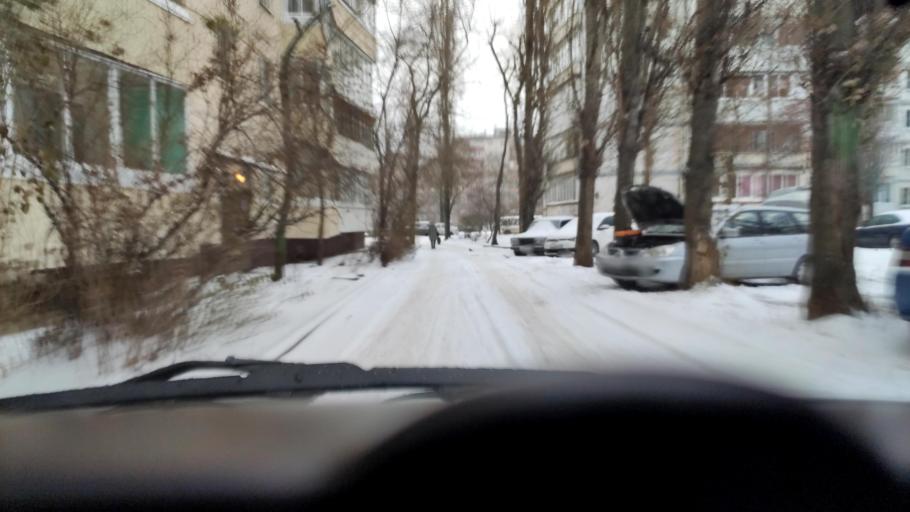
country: RU
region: Voronezj
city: Pridonskoy
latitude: 51.6528
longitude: 39.1185
